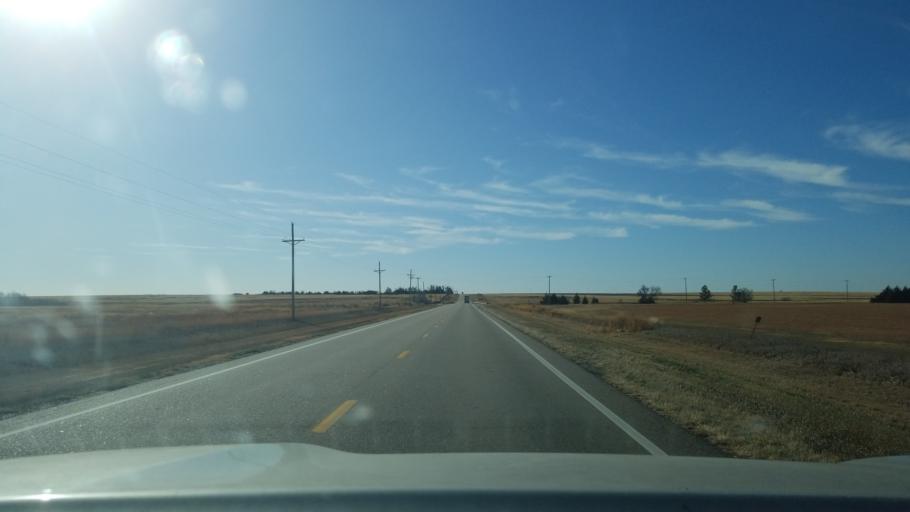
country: US
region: Kansas
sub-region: Ness County
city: Ness City
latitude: 38.4101
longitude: -99.8985
